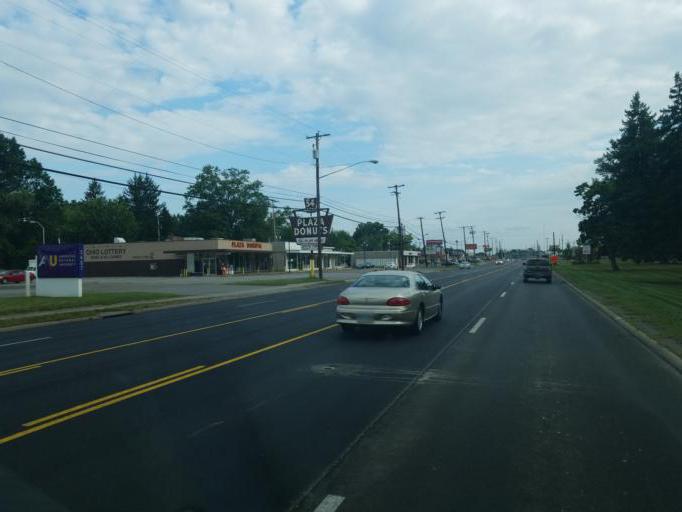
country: US
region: Ohio
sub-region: Trumbull County
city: Churchill
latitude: 41.1444
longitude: -80.6655
